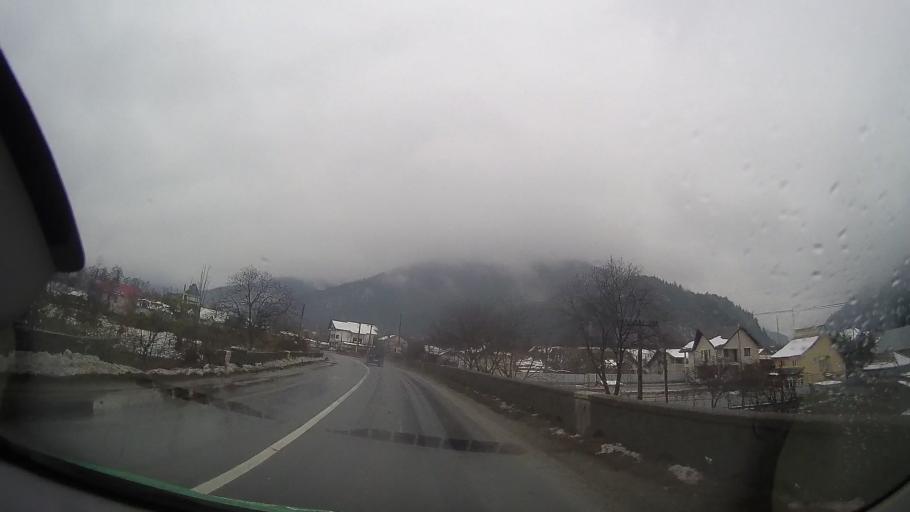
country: RO
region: Neamt
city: Viisoara
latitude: 46.9312
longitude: 26.2200
